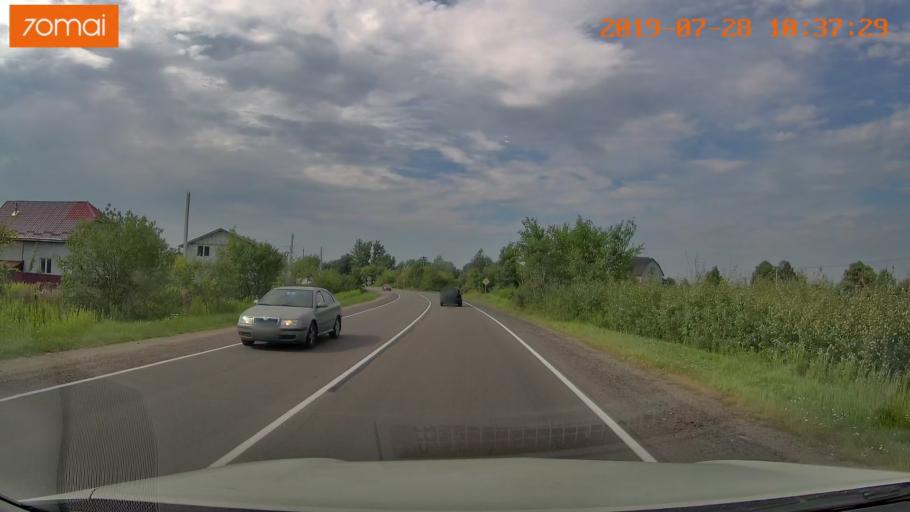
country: RU
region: Kaliningrad
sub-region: Gorod Kaliningrad
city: Kaliningrad
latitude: 54.7310
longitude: 20.4077
